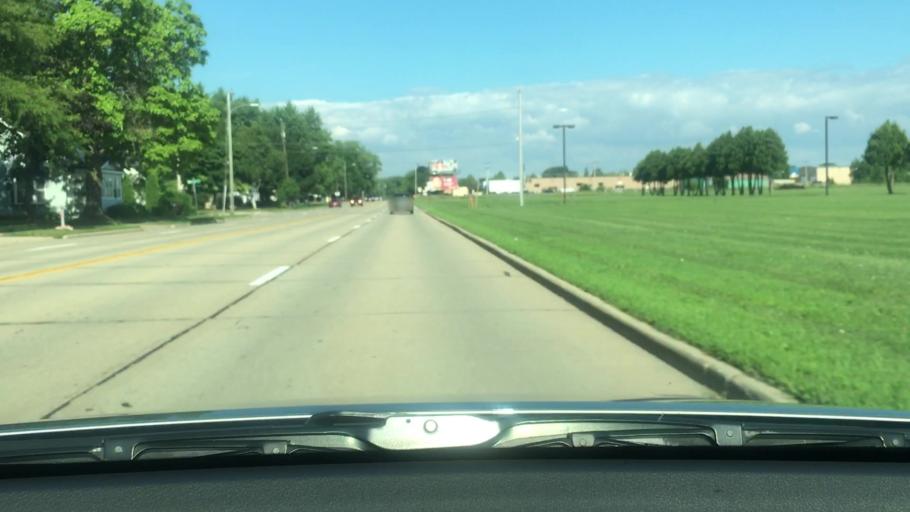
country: US
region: Wisconsin
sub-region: Winnebago County
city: Oshkosh
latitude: 43.9958
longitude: -88.5510
